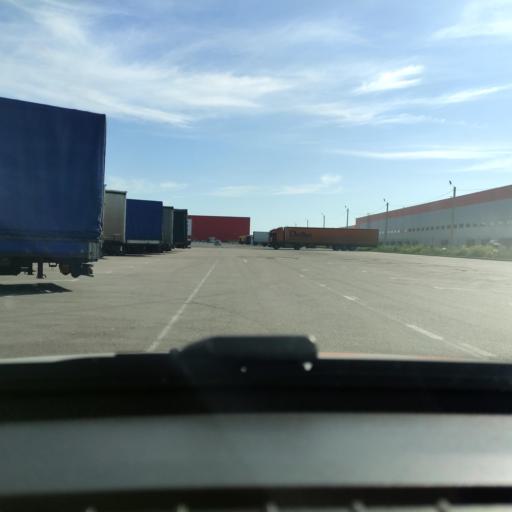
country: RU
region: Voronezj
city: Podgornoye
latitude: 51.8057
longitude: 39.2204
